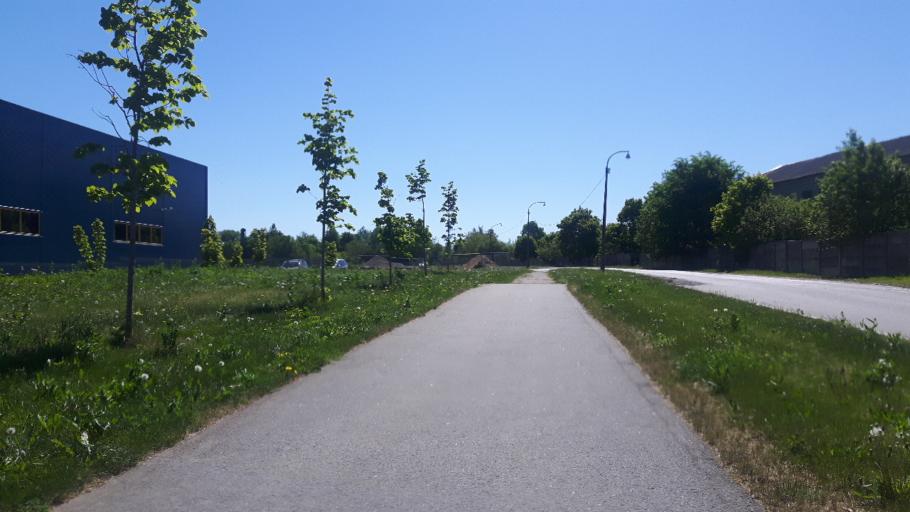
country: EE
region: Ida-Virumaa
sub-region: Sillamaee linn
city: Sillamae
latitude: 59.3971
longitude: 27.7482
